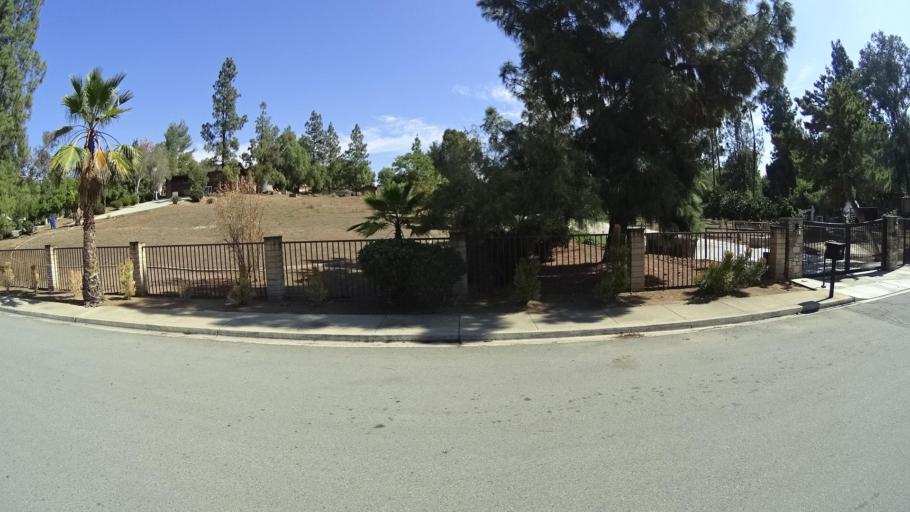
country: US
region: California
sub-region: San Diego County
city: Granite Hills
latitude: 32.7839
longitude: -116.9007
